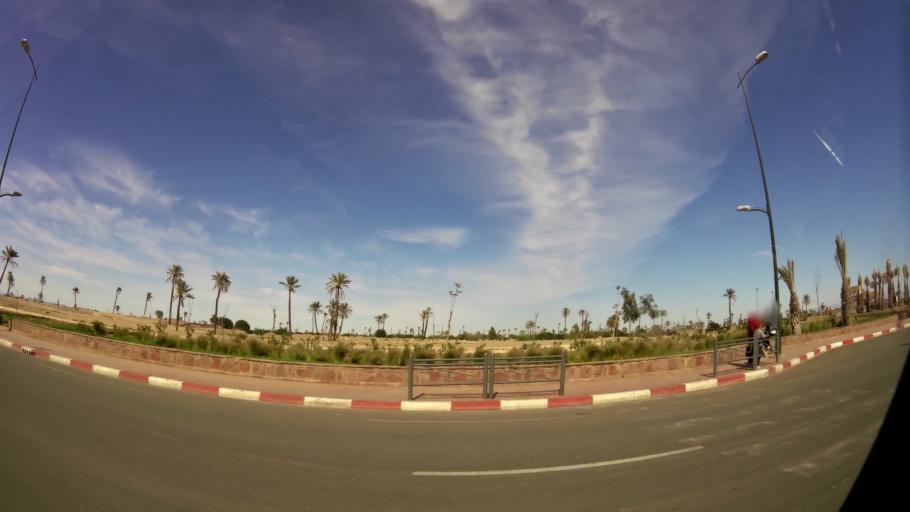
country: MA
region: Marrakech-Tensift-Al Haouz
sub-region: Marrakech
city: Marrakesh
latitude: 31.6306
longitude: -7.9732
